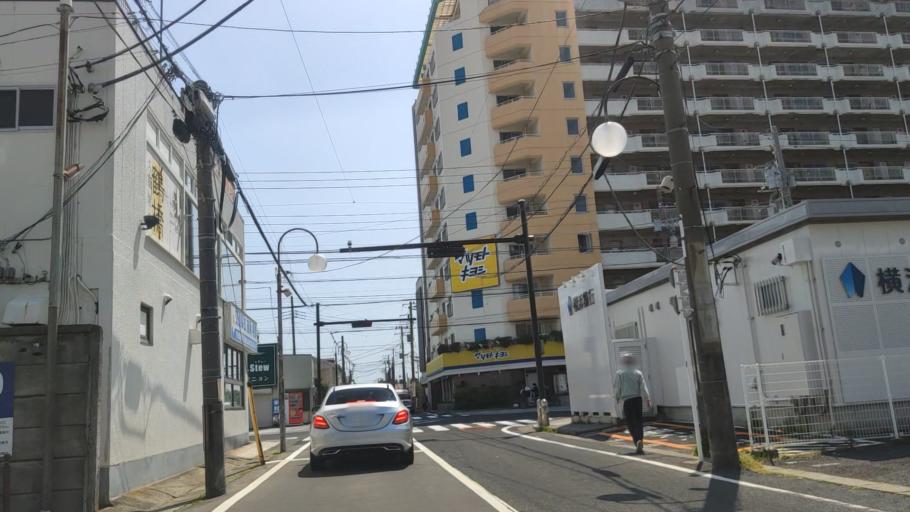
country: JP
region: Kanagawa
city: Hiratsuka
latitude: 35.3188
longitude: 139.3392
